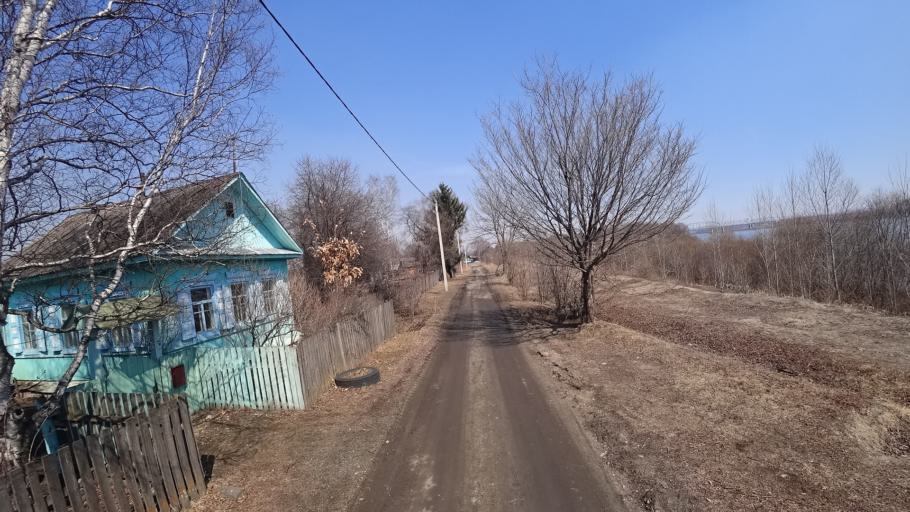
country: RU
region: Amur
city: Novobureyskiy
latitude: 49.7782
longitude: 129.8514
